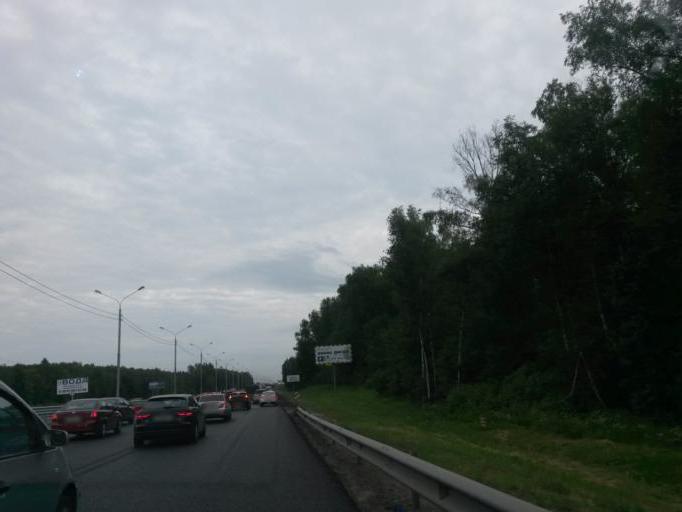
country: RU
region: Moskovskaya
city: Lyubuchany
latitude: 55.2687
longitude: 37.5365
